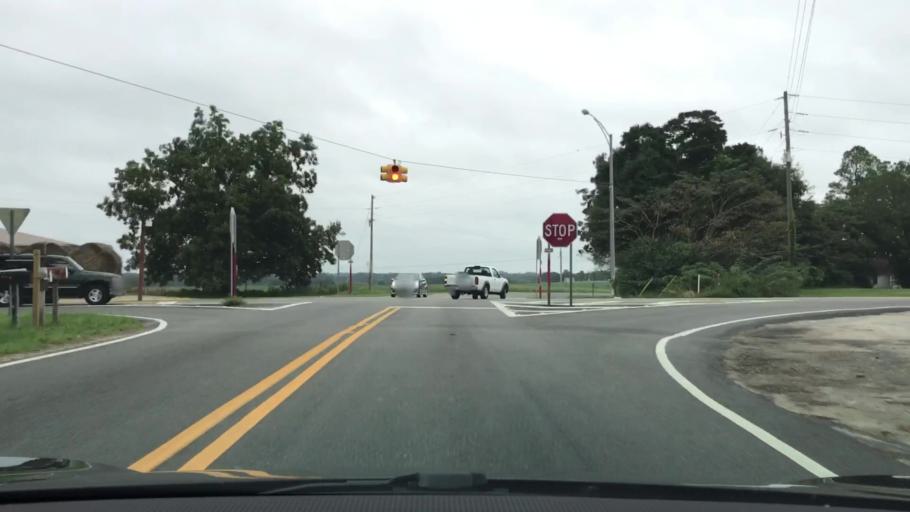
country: US
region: Alabama
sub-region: Covington County
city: Opp
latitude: 31.2802
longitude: -86.1572
